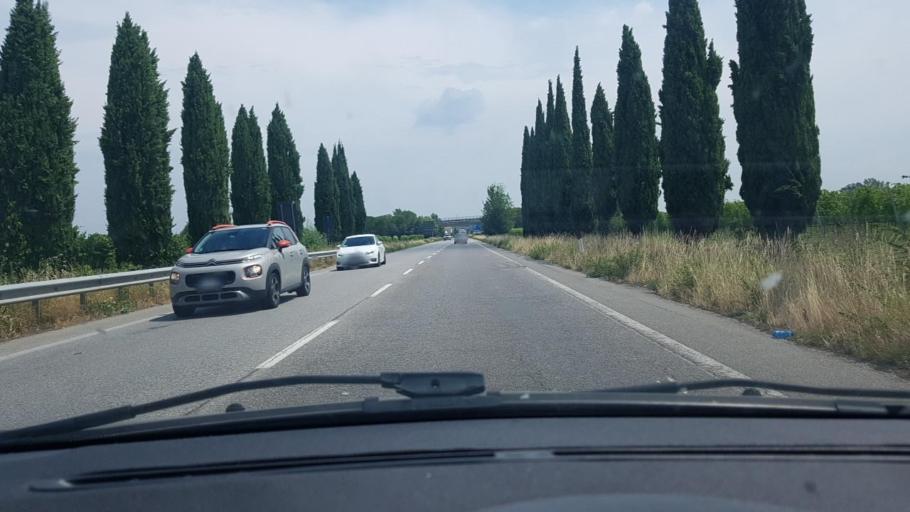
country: IT
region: Lombardy
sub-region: Provincia di Brescia
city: San Martino della Battaglia
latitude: 45.4449
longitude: 10.6037
